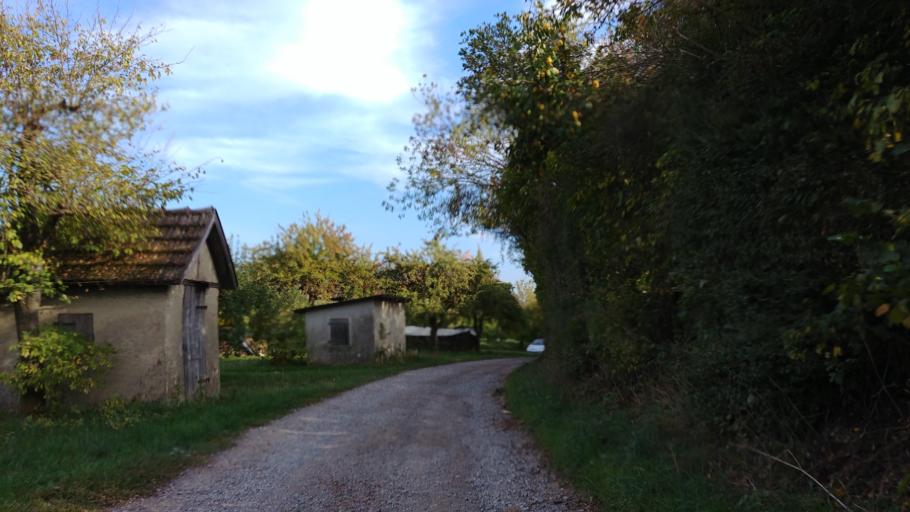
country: DE
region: Baden-Wuerttemberg
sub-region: Regierungsbezirk Stuttgart
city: Ilsfeld
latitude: 49.0689
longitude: 9.2482
